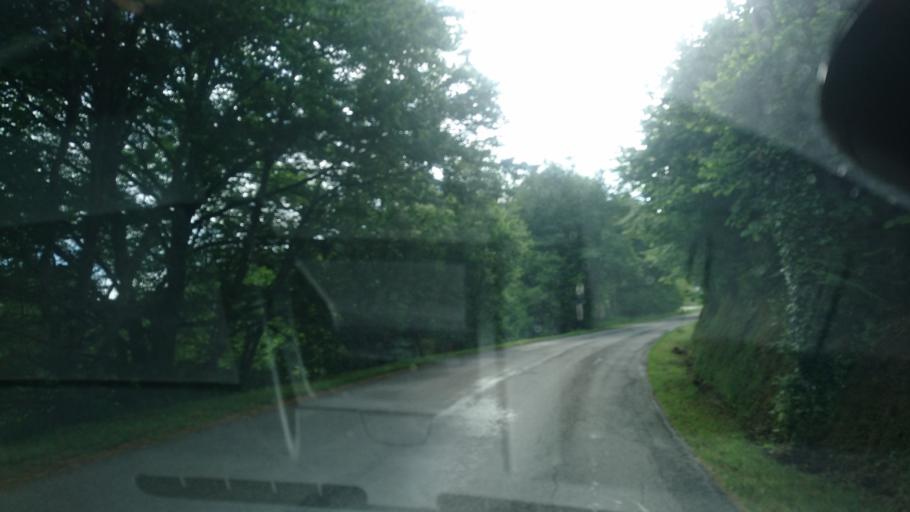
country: FR
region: Limousin
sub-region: Departement de la Haute-Vienne
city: Peyrat-le-Chateau
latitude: 45.8109
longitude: 1.7844
